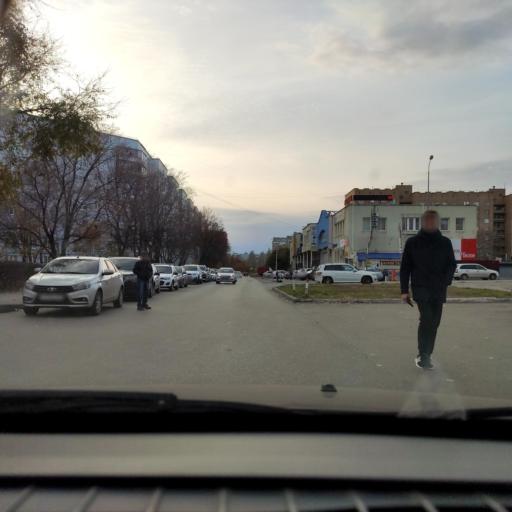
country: RU
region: Samara
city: Tol'yatti
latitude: 53.5331
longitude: 49.3193
